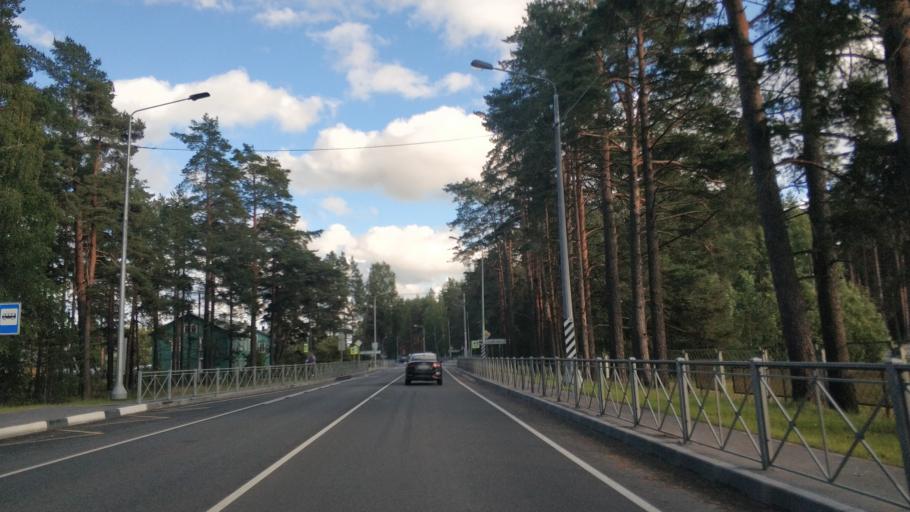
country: RU
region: Leningrad
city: Priozersk
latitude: 61.0182
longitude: 30.1373
